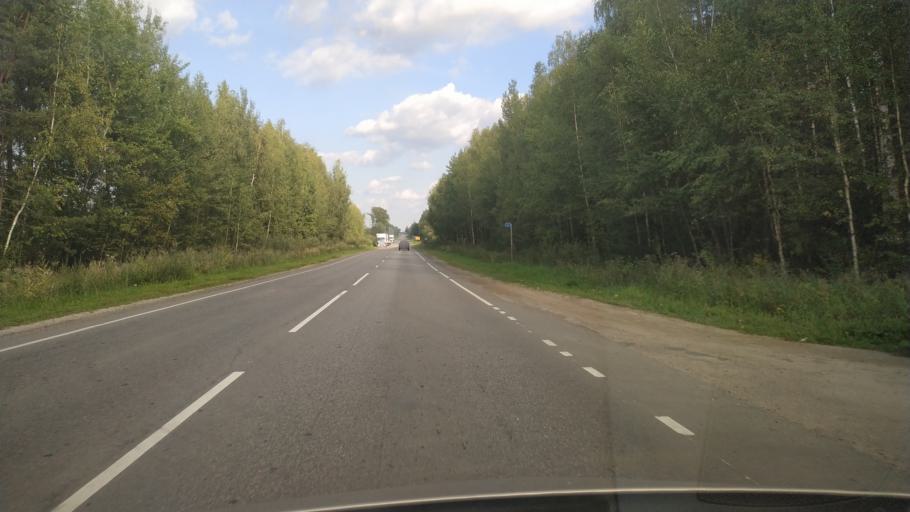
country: RU
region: Moskovskaya
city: Vereya
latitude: 55.7087
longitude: 39.0866
